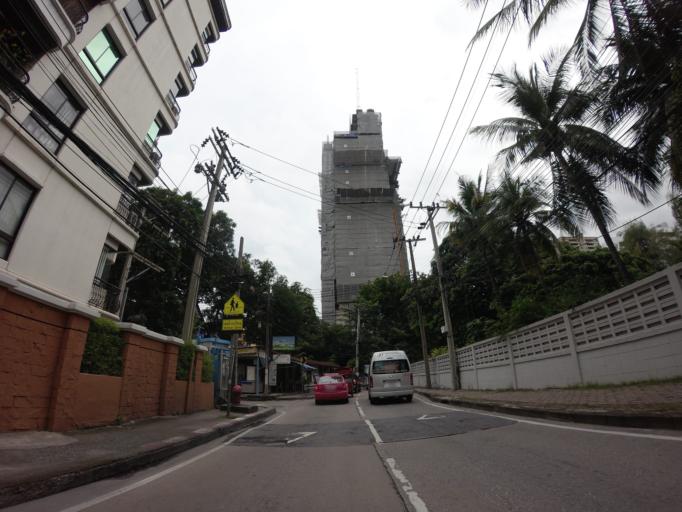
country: TH
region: Bangkok
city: Watthana
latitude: 13.7385
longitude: 100.5725
